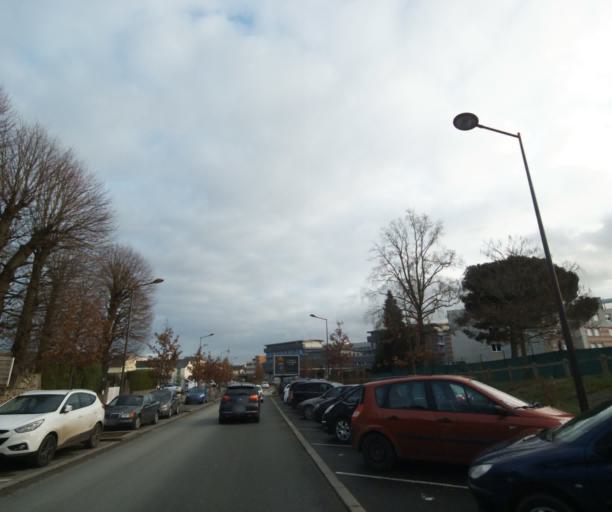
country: FR
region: Pays de la Loire
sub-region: Departement de la Sarthe
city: Coulaines
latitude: 48.0167
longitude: 0.1785
